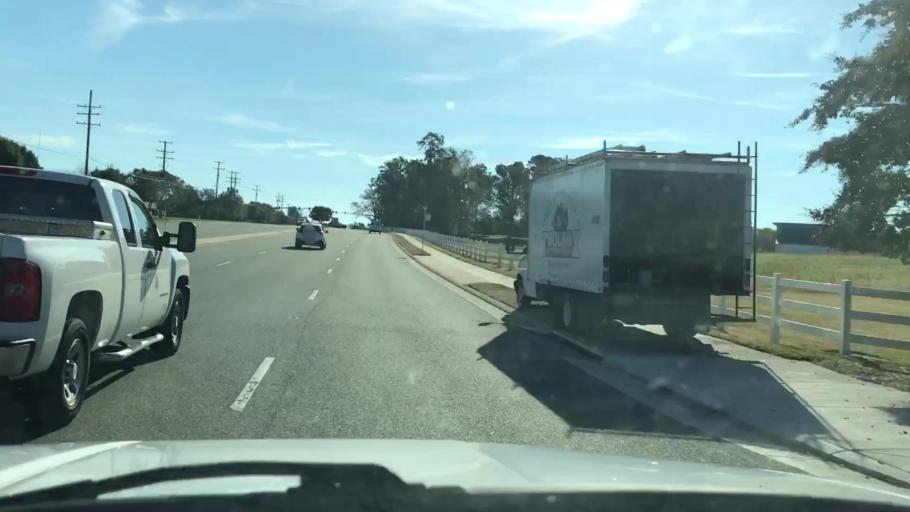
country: US
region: Virginia
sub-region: Henrico County
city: Short Pump
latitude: 37.6583
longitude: -77.6326
